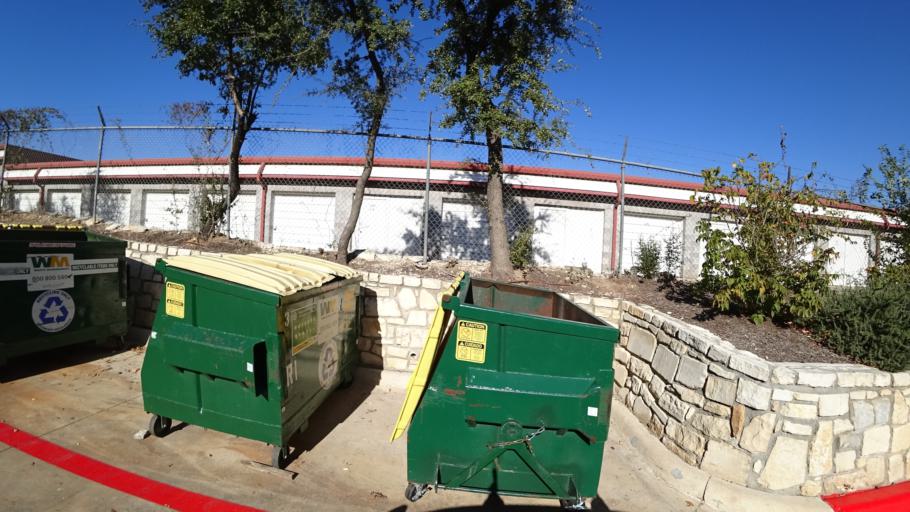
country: US
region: Texas
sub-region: Travis County
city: Rollingwood
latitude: 30.2437
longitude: -97.7803
